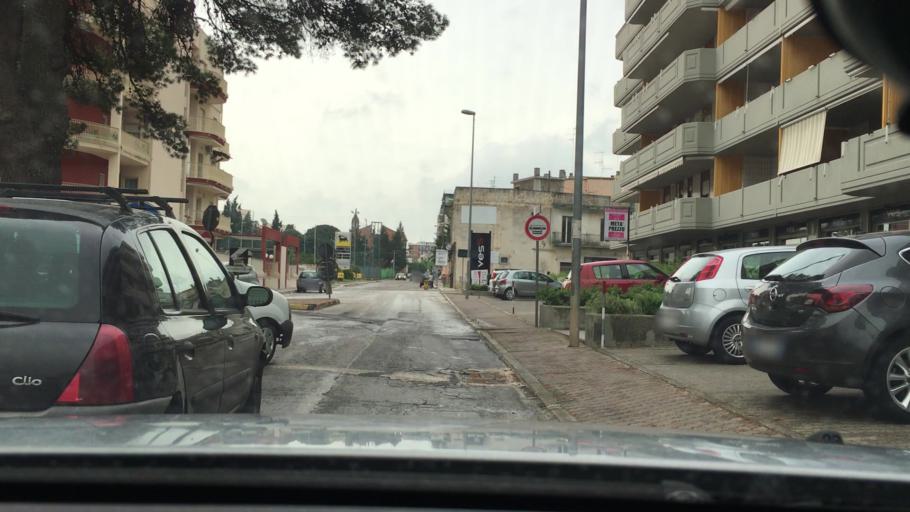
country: IT
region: Apulia
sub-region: Provincia di Bari
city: Gioia del Colle
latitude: 40.8069
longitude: 16.9243
